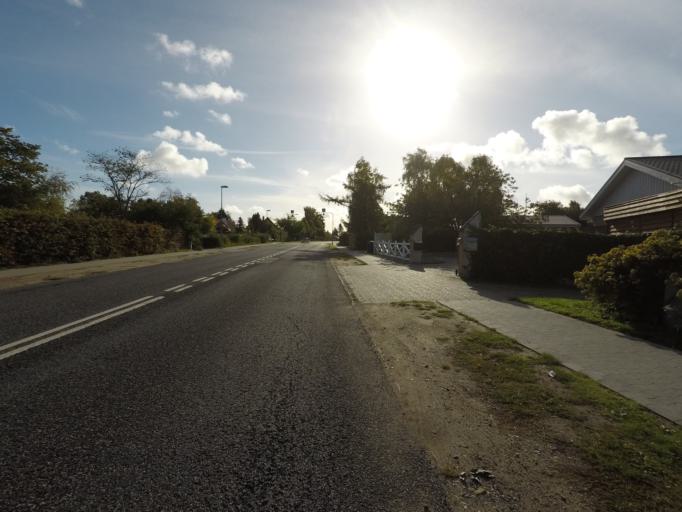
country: DK
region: Capital Region
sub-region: Egedal Kommune
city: Smorumnedre
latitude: 55.7385
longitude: 12.2926
